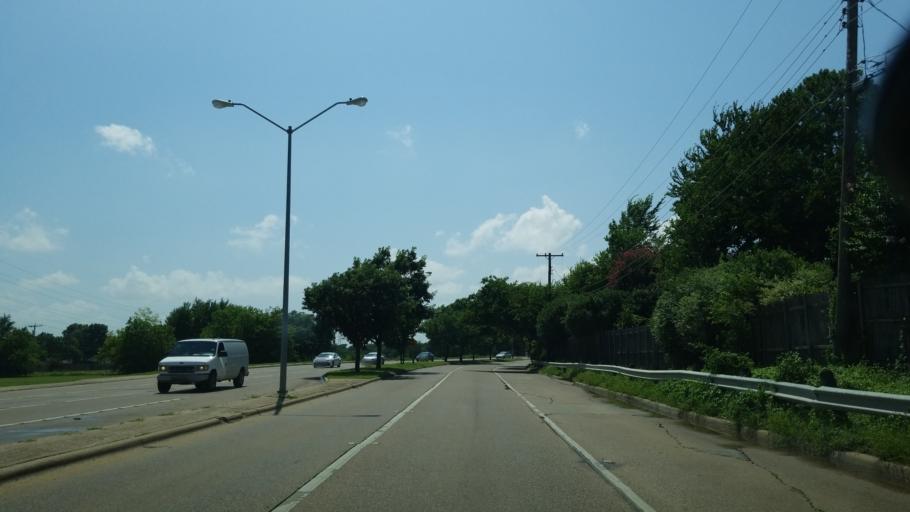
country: US
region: Texas
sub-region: Dallas County
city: Farmers Branch
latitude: 32.8860
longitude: -96.8680
